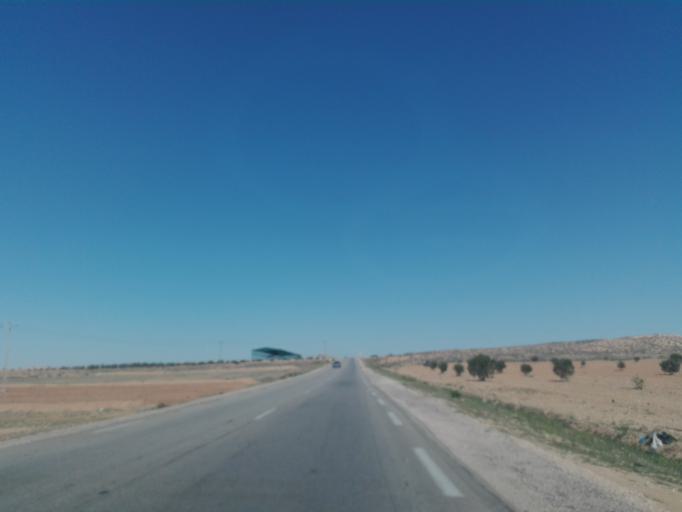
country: TN
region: Safaqis
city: Bi'r `Ali Bin Khalifah
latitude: 34.7332
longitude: 10.4198
